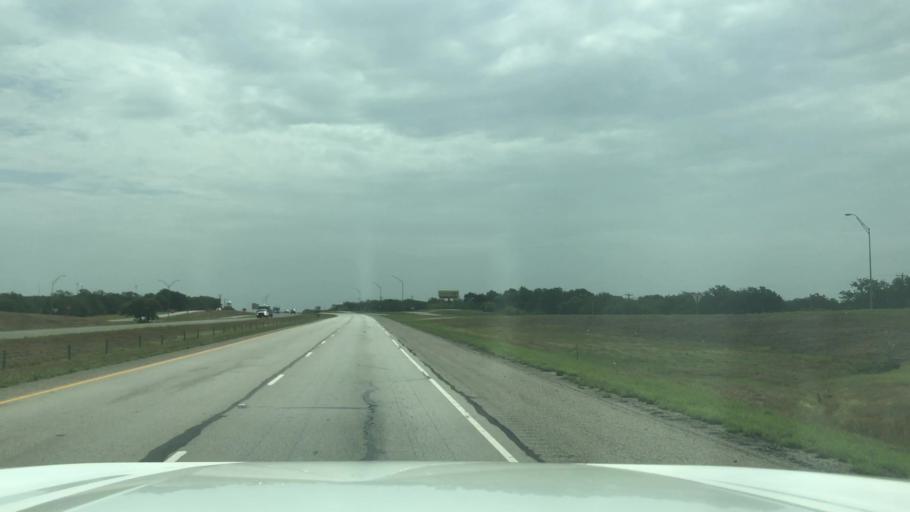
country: US
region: Texas
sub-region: Eastland County
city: Cisco
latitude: 32.3750
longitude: -99.0043
